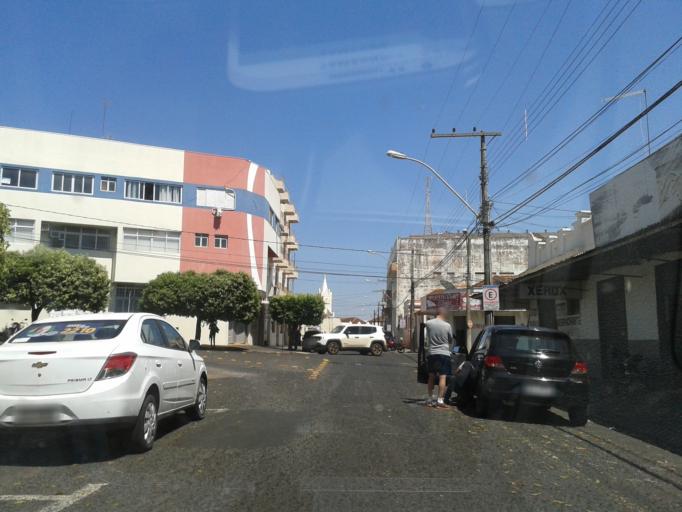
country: BR
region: Minas Gerais
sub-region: Araguari
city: Araguari
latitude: -18.6488
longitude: -48.1884
